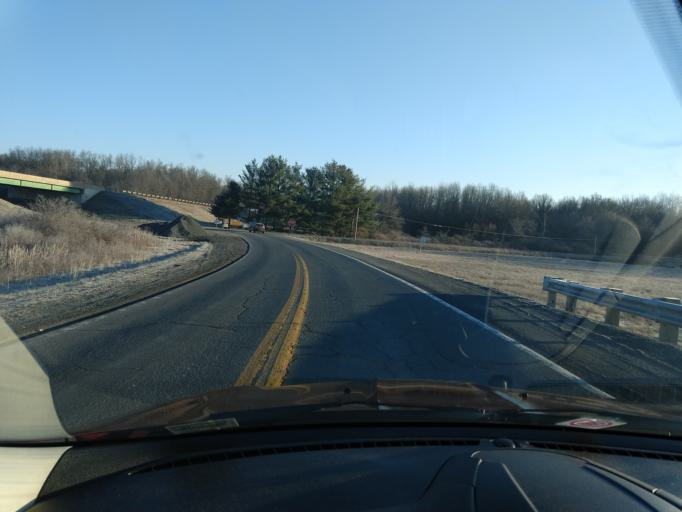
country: US
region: West Virginia
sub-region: Greenbrier County
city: Rainelle
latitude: 37.8569
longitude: -80.7172
